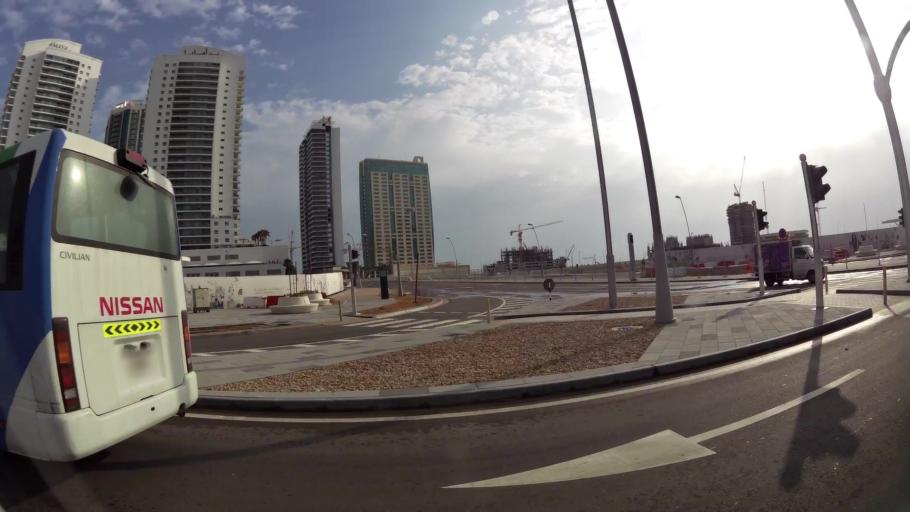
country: AE
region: Abu Dhabi
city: Abu Dhabi
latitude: 24.5089
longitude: 54.4052
